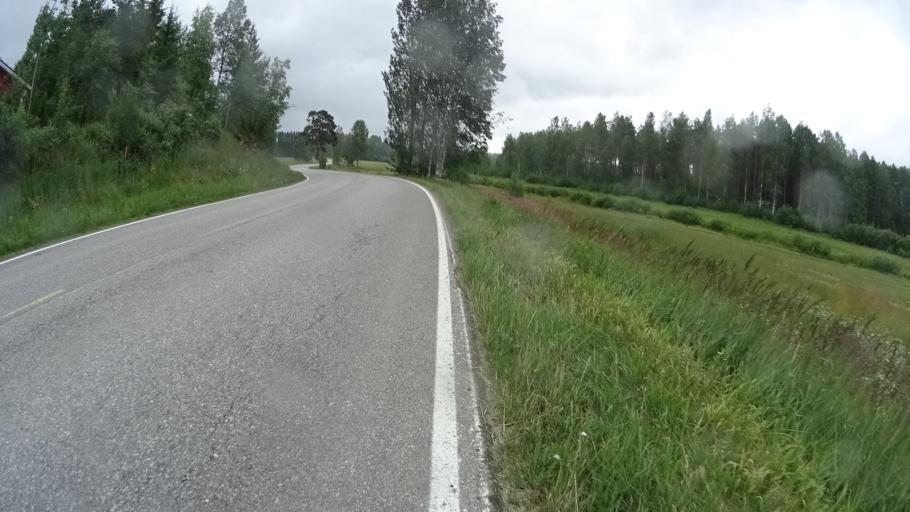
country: FI
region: Uusimaa
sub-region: Helsinki
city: Karkkila
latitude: 60.5809
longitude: 24.3358
